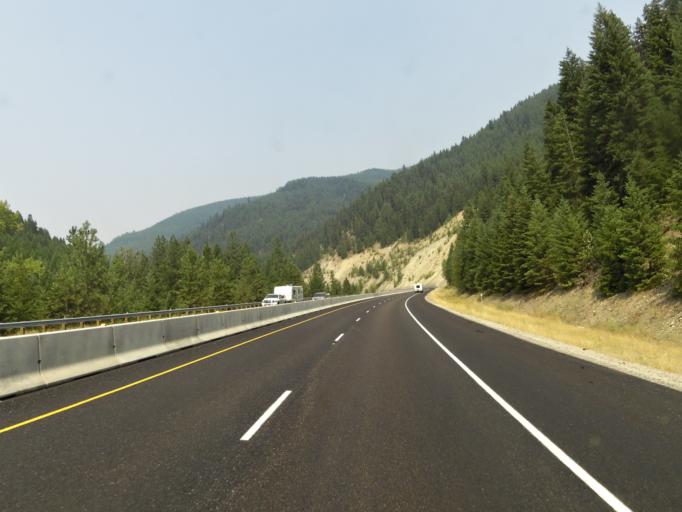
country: US
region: Montana
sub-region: Sanders County
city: Thompson Falls
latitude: 47.3087
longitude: -115.2077
